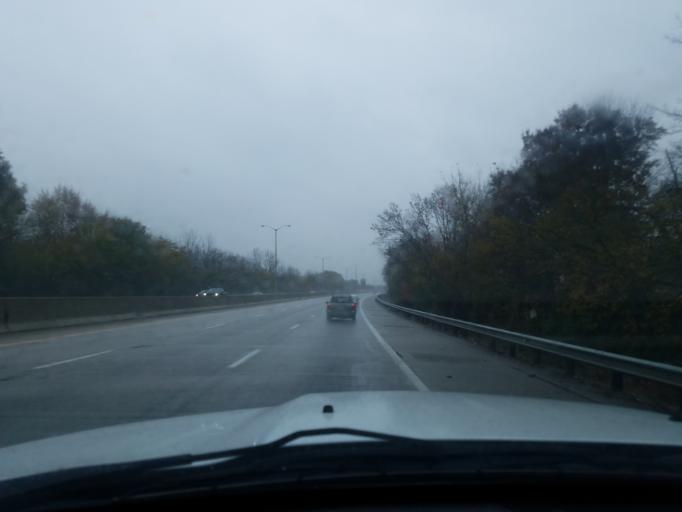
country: US
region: Kentucky
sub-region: Jefferson County
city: Shively
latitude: 38.1995
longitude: -85.8278
